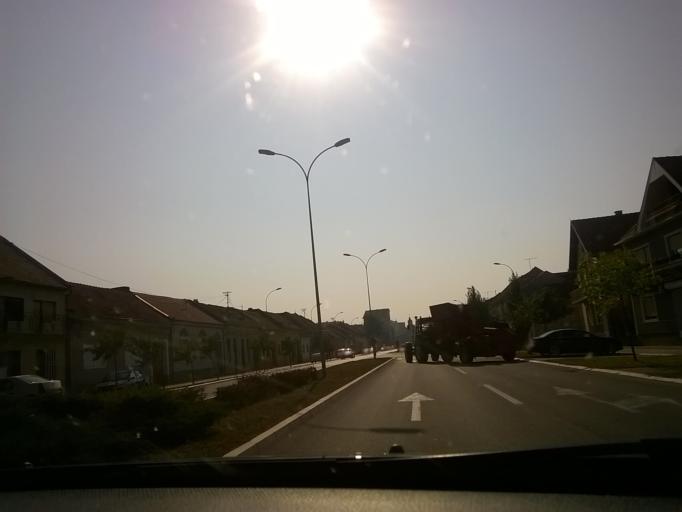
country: RS
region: Autonomna Pokrajina Vojvodina
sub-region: Juznobanatski Okrug
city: Vrsac
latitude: 45.1249
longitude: 21.2930
